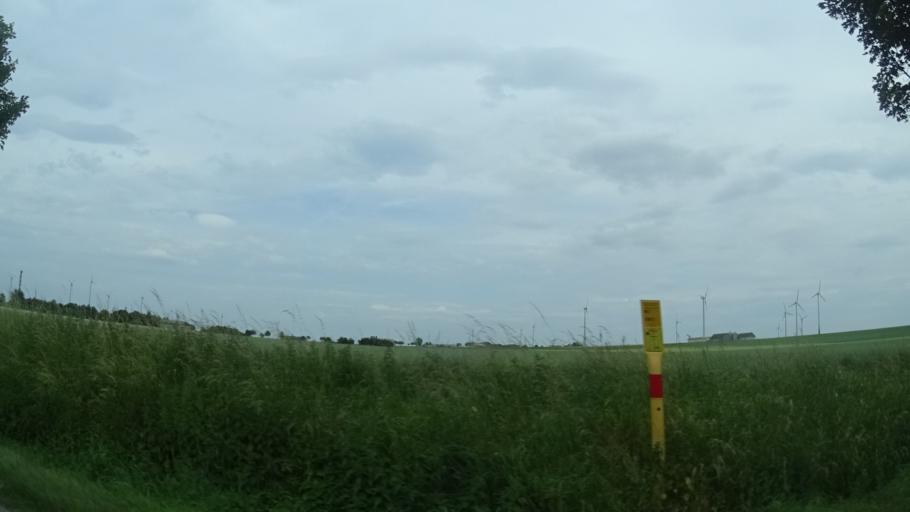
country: DE
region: North Rhine-Westphalia
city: Warburg
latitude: 51.5894
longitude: 9.1327
